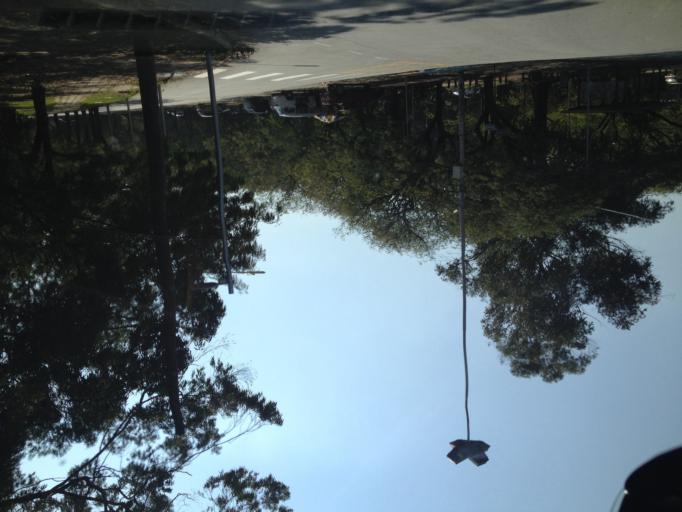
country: BR
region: Sao Paulo
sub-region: Osasco
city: Osasco
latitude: -23.5608
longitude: -46.7198
